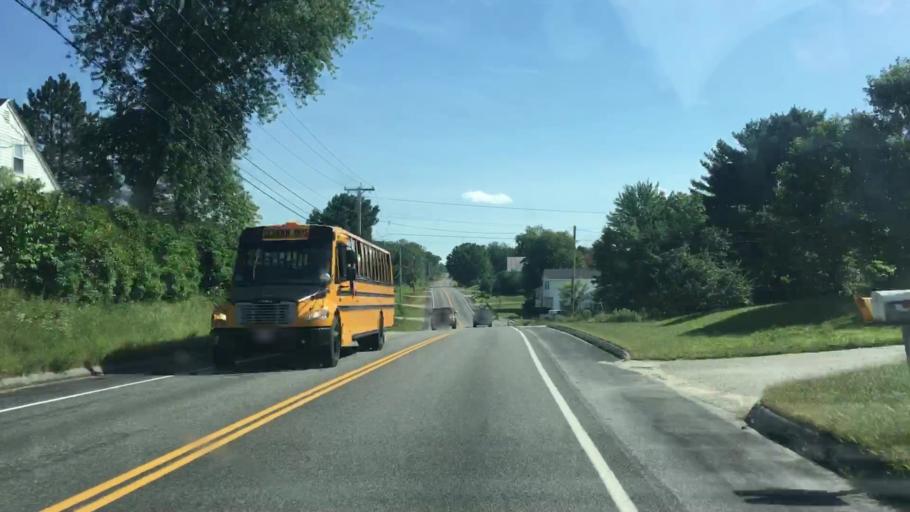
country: US
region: Maine
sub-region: Androscoggin County
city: Sabattus
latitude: 44.0996
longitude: -70.0854
